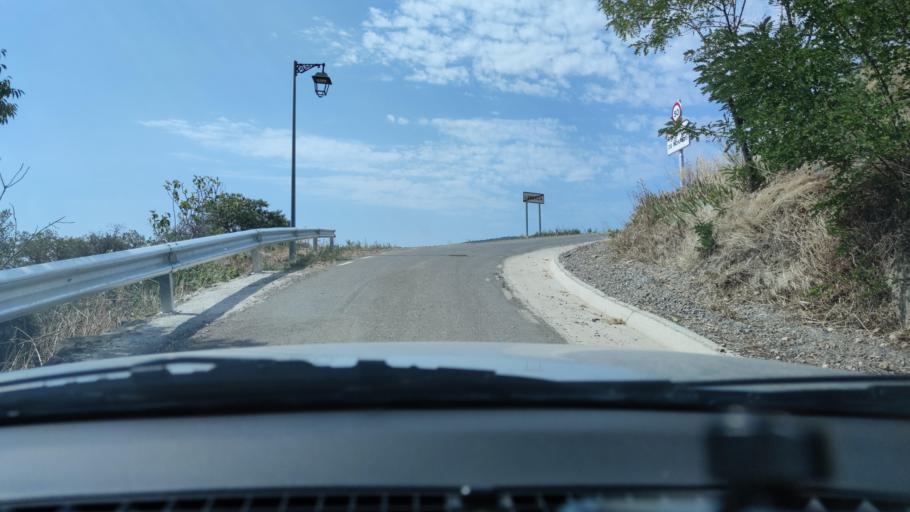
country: ES
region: Catalonia
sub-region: Provincia de Lleida
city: Ager
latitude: 42.0128
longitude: 0.8261
